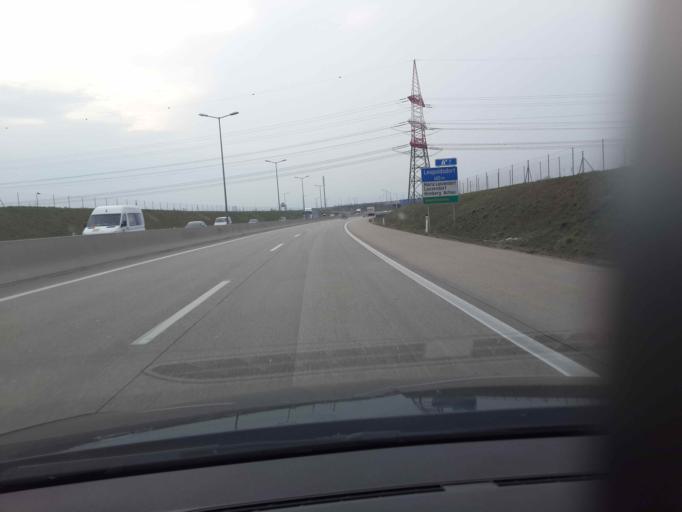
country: AT
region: Lower Austria
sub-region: Politischer Bezirk Wien-Umgebung
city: Lanzendorf
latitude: 48.1202
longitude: 16.4188
